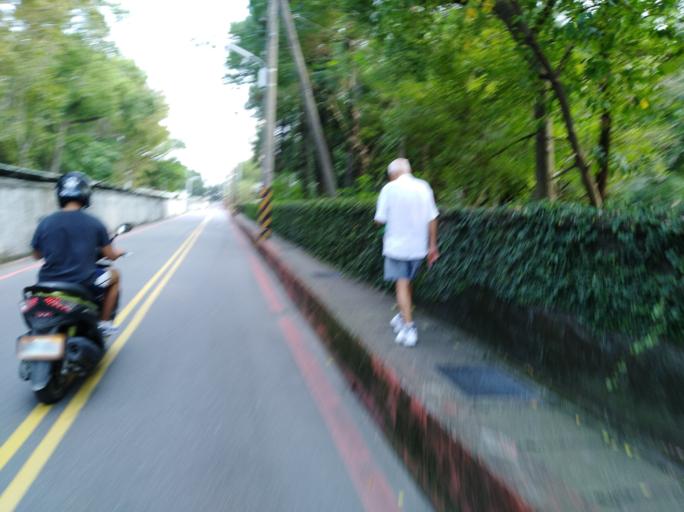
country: TW
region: Taipei
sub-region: Taipei
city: Banqiao
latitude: 25.0358
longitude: 121.4289
